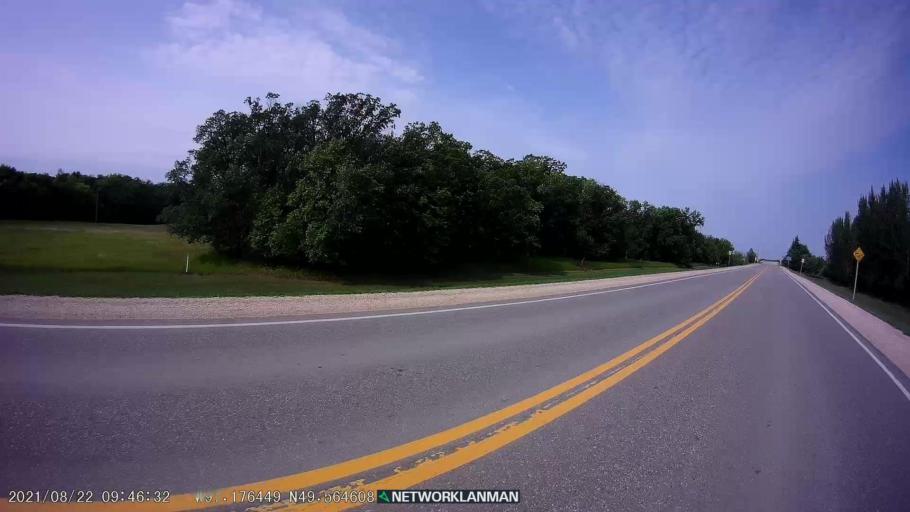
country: CA
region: Manitoba
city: Niverville
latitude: 49.5647
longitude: -97.1769
